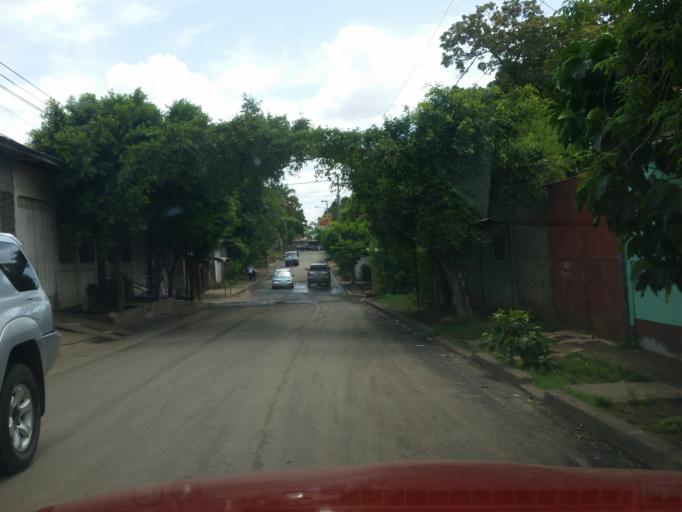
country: NI
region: Managua
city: Managua
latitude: 12.1057
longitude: -86.2316
